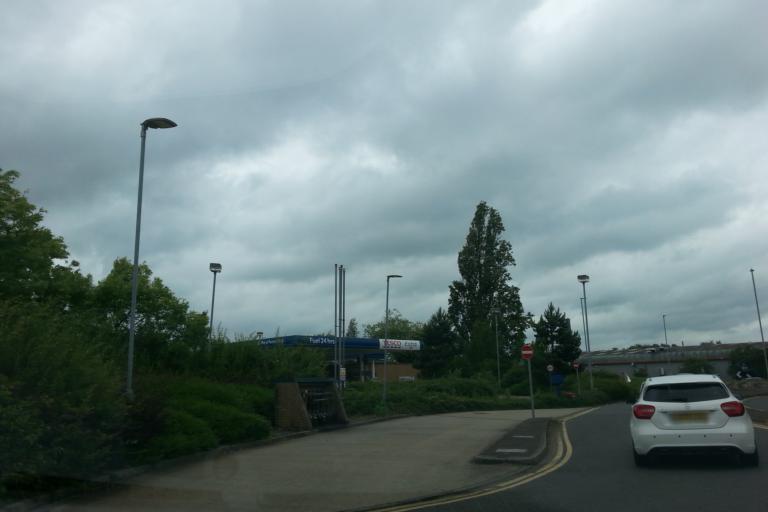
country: GB
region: England
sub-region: Cambridgeshire
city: Swavesey
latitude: 52.2548
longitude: 0.0196
